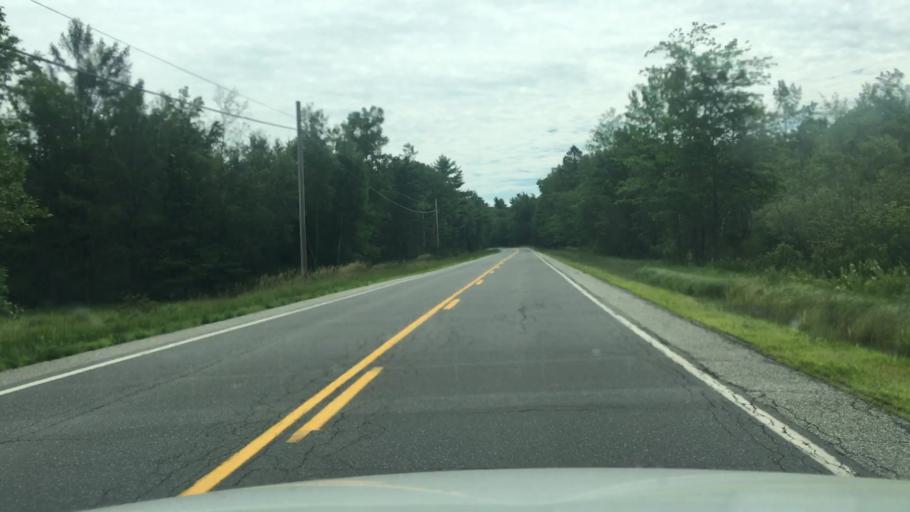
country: US
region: Maine
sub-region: Kennebec County
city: Clinton
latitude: 44.6143
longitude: -69.4296
